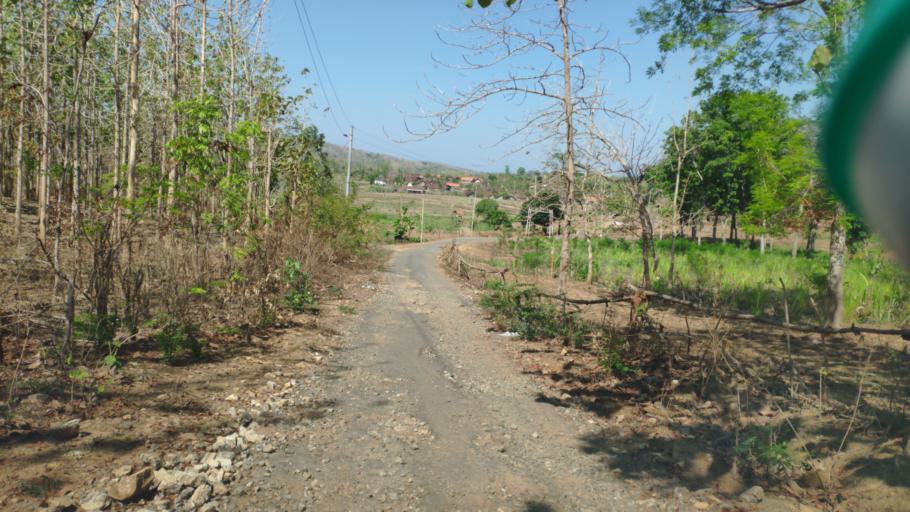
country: ID
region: East Java
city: Krajan Jamprong
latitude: -6.9895
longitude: 111.6175
